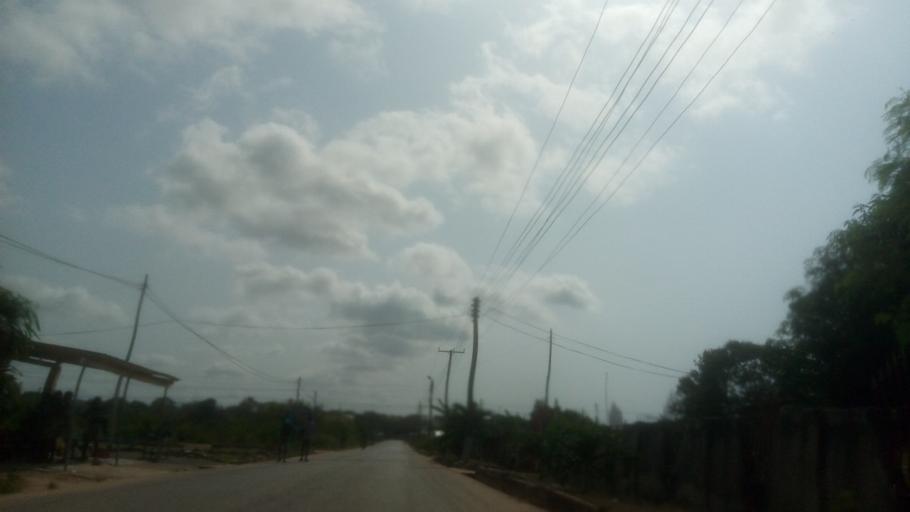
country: GH
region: Central
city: Winneba
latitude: 5.3570
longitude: -0.6357
